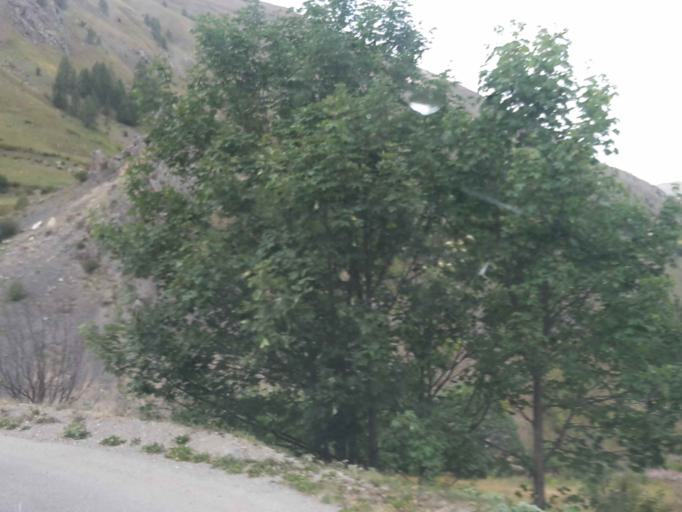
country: FR
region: Rhone-Alpes
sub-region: Departement de la Savoie
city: Valloire
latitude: 45.1241
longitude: 6.4190
